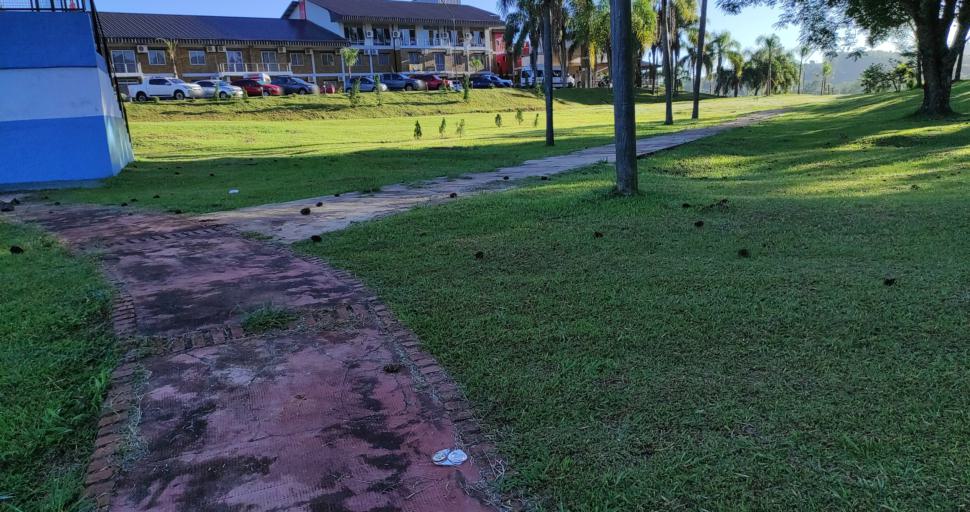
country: AR
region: Misiones
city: Dos de Mayo
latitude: -27.0440
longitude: -54.6842
